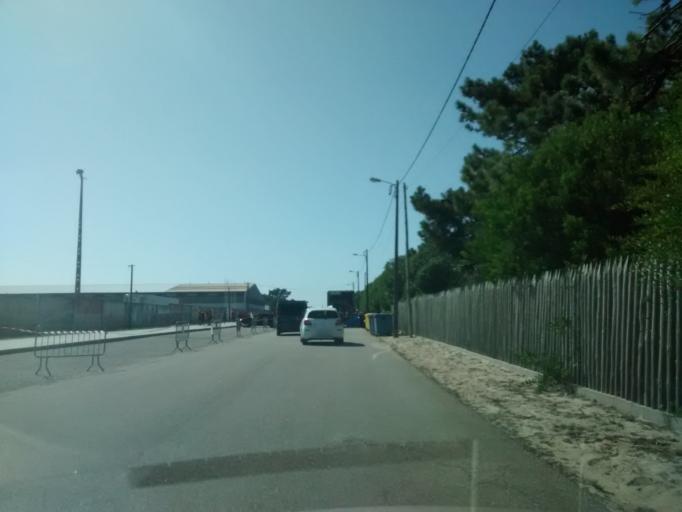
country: PT
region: Aveiro
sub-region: Ilhavo
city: Gafanha da Nazare
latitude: 40.6666
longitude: -8.7371
